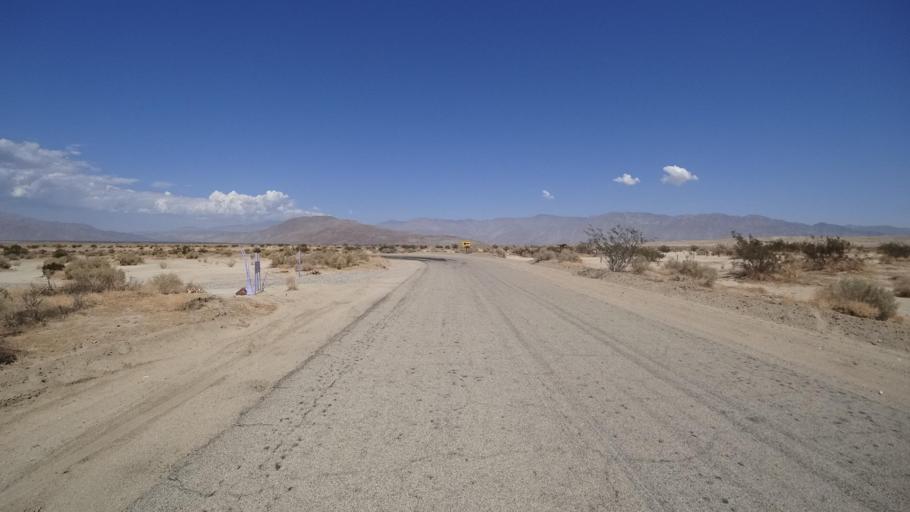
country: US
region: California
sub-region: San Diego County
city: Borrego Springs
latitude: 33.2571
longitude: -116.2953
